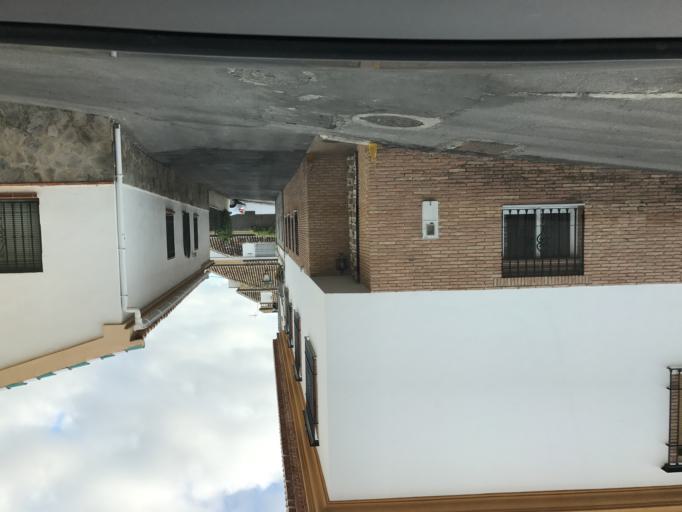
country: ES
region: Andalusia
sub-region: Provincia de Granada
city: Cajar
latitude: 37.1241
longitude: -3.5670
